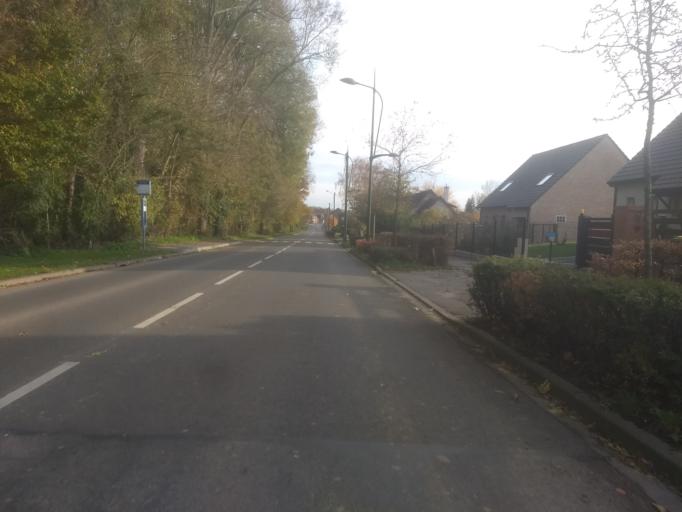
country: FR
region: Nord-Pas-de-Calais
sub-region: Departement du Pas-de-Calais
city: Agny
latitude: 50.2639
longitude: 2.7530
